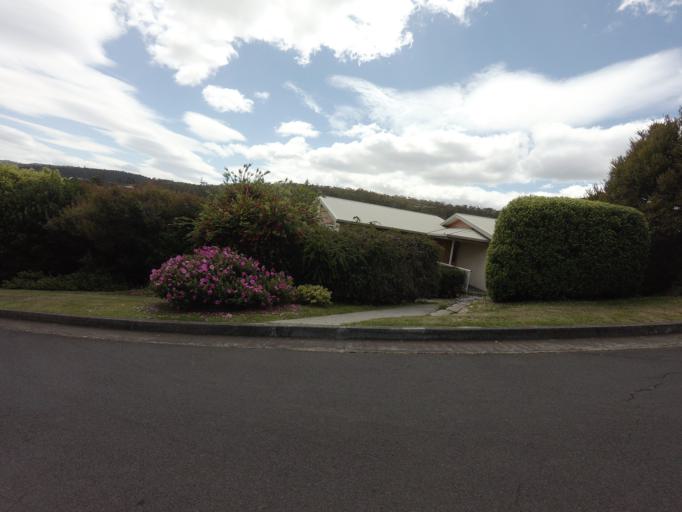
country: AU
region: Tasmania
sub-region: Clarence
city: Howrah
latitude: -42.8876
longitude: 147.4149
